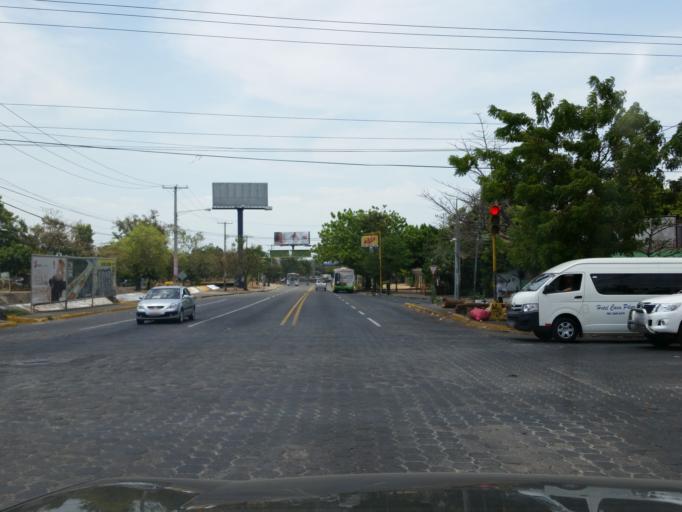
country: NI
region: Managua
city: Managua
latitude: 12.1461
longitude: -86.2412
